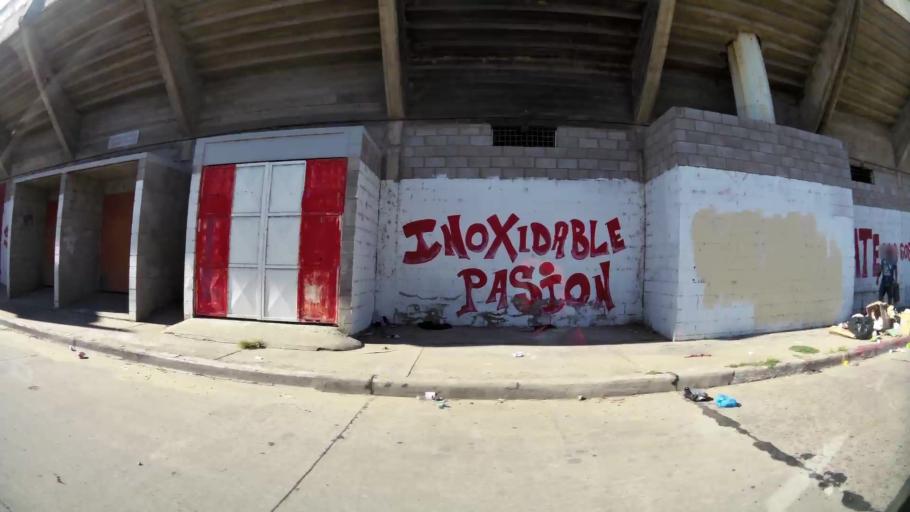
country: AR
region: Santa Fe
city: Santa Fe de la Vera Cruz
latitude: -31.6313
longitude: -60.7159
